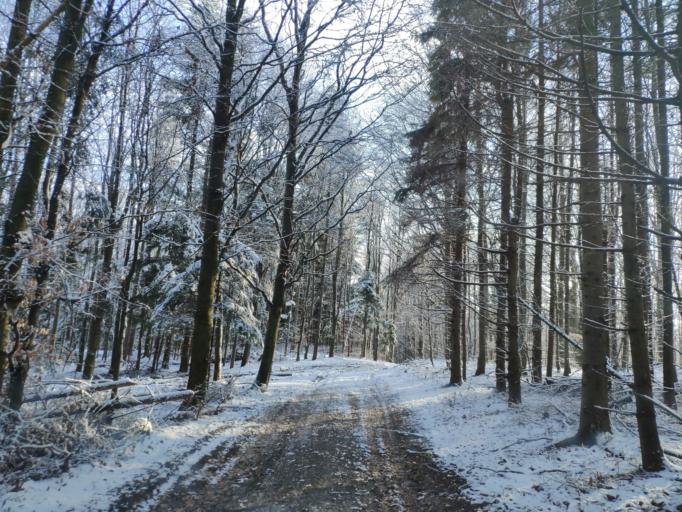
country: SK
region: Kosicky
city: Moldava nad Bodvou
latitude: 48.7437
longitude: 21.0877
